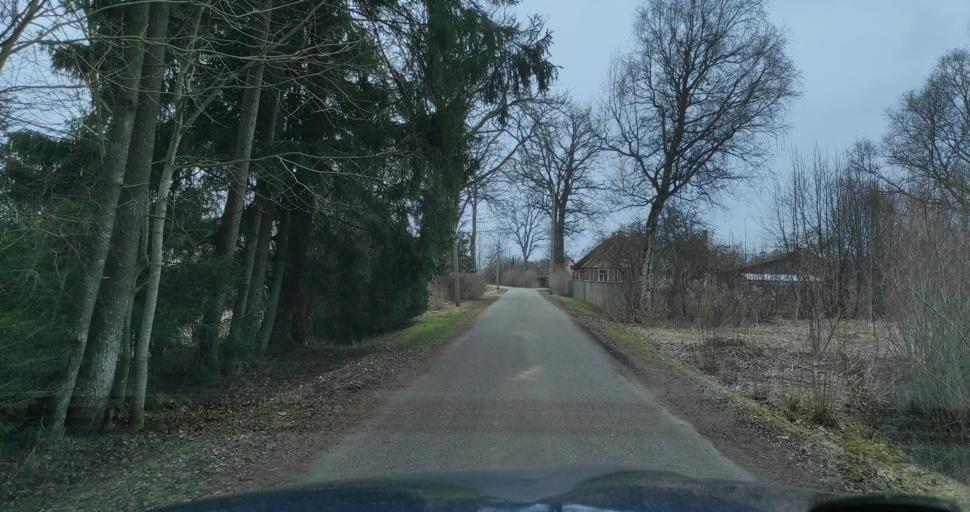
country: LV
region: Ventspils Rajons
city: Piltene
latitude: 57.2221
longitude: 21.6885
